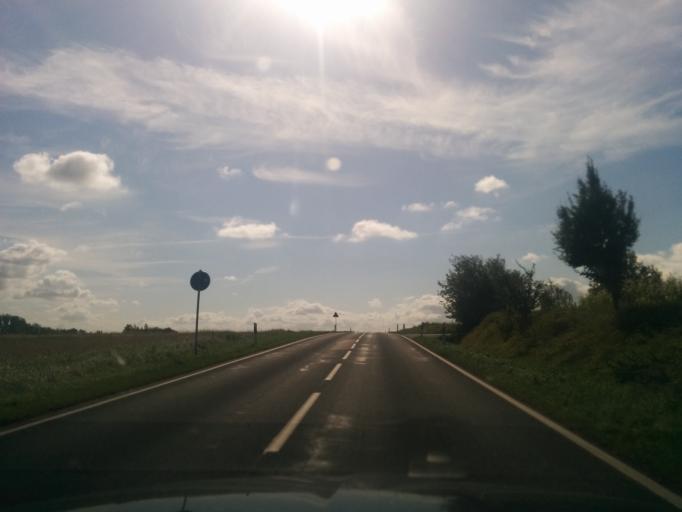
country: DE
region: Saxony-Anhalt
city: Salzmunde
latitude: 51.5241
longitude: 11.8394
